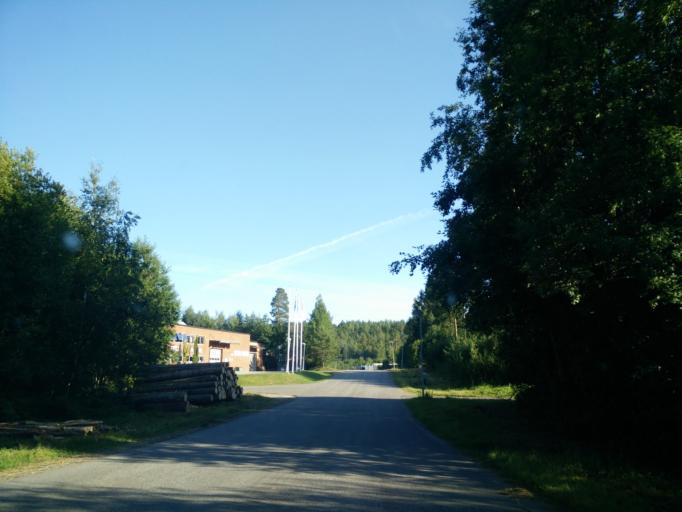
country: SE
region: Vaesternorrland
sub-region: Sundsvalls Kommun
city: Sundsvall
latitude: 62.4084
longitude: 17.2840
